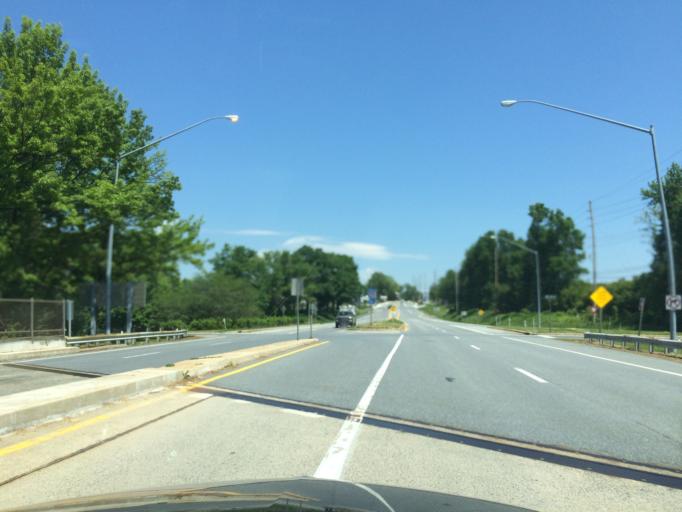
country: US
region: Maryland
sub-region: Frederick County
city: Myersville
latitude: 39.4966
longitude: -77.5680
